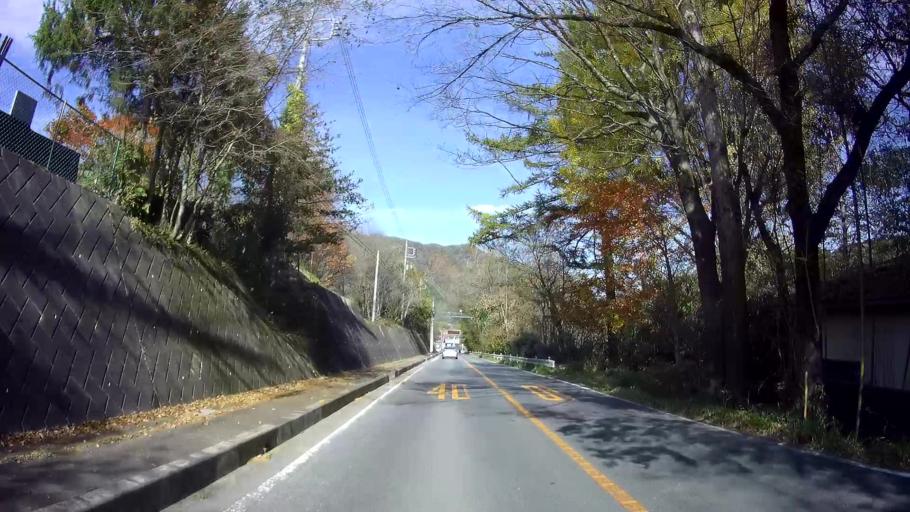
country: JP
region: Gunma
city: Nakanojomachi
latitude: 36.5074
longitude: 138.7755
